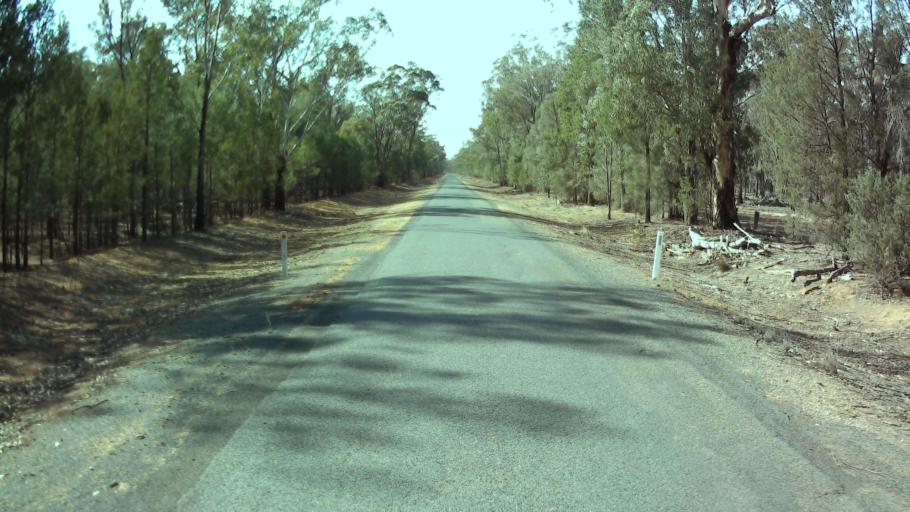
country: AU
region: New South Wales
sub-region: Weddin
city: Grenfell
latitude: -33.7145
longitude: 148.0246
